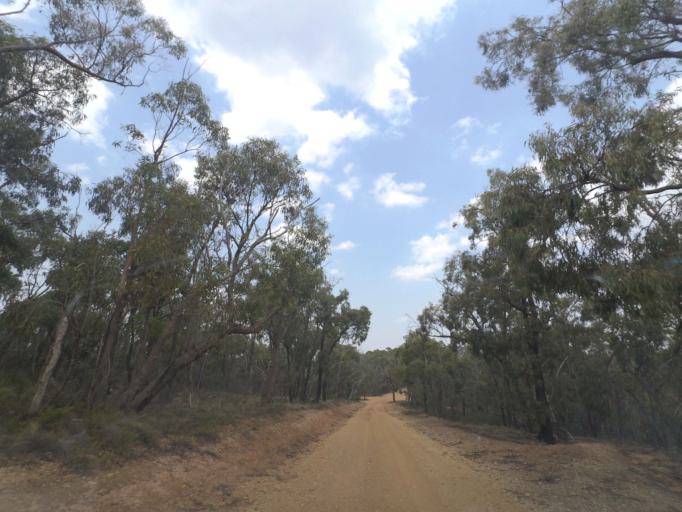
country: AU
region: Victoria
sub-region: Moorabool
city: Bacchus Marsh
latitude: -37.5818
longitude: 144.4412
